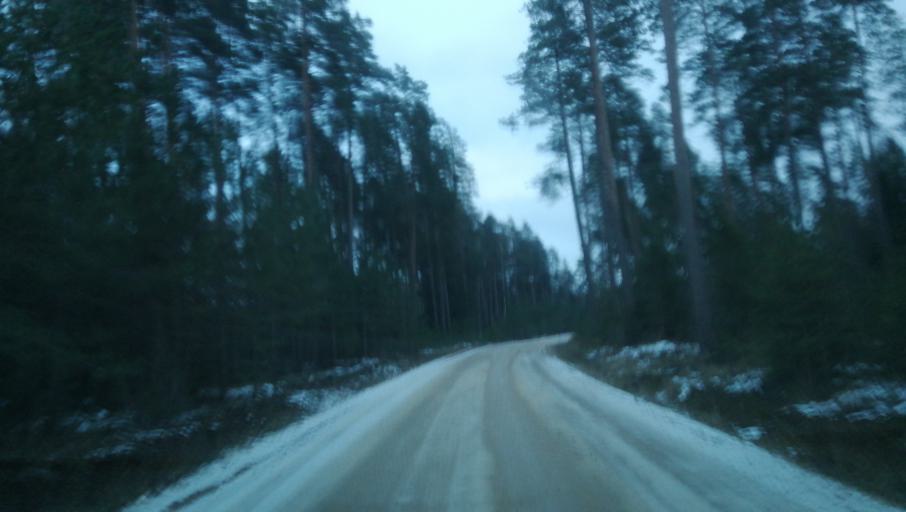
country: LV
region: Garkalne
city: Garkalne
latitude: 57.0277
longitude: 24.3843
